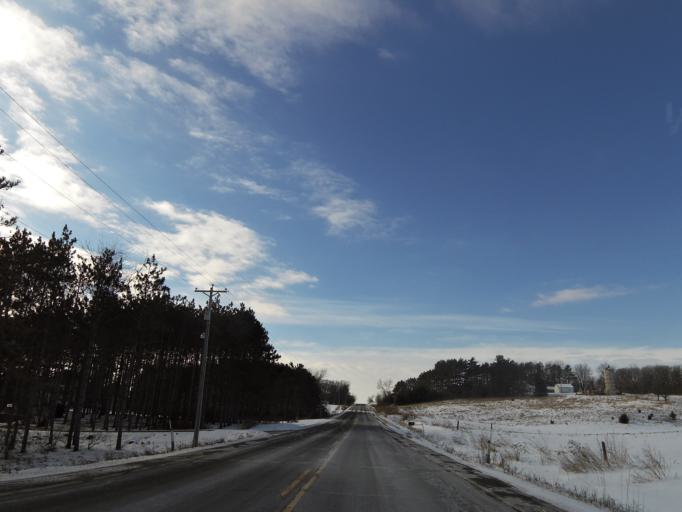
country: US
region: Wisconsin
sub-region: Saint Croix County
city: Roberts
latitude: 44.9927
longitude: -92.5862
